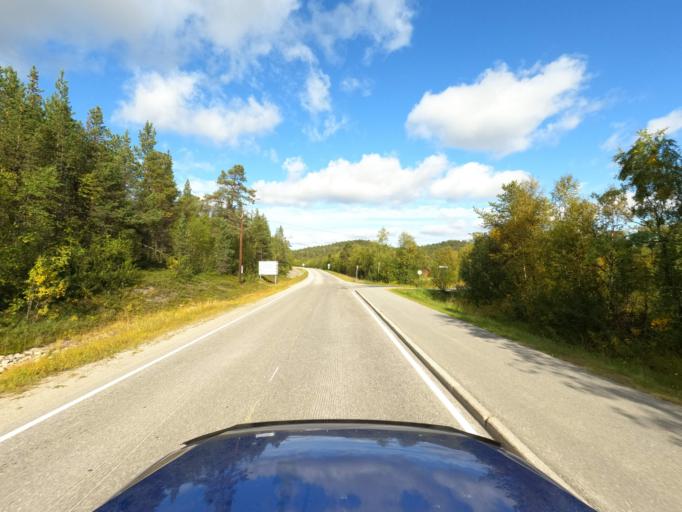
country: NO
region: Finnmark Fylke
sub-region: Karasjok
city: Karasjohka
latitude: 69.4779
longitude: 25.5171
